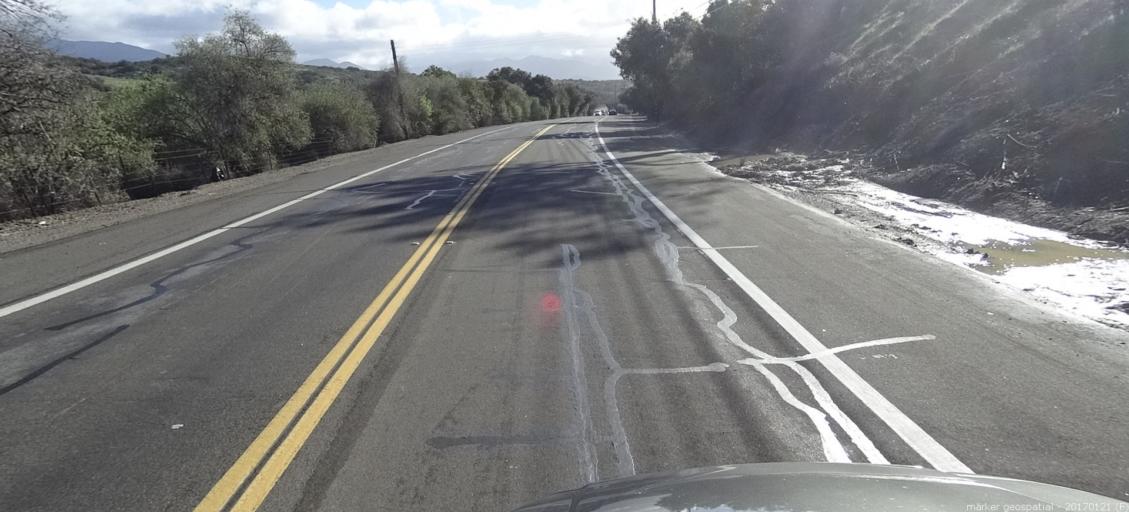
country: US
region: California
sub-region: Orange County
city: North Tustin
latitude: 33.7617
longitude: -117.7079
